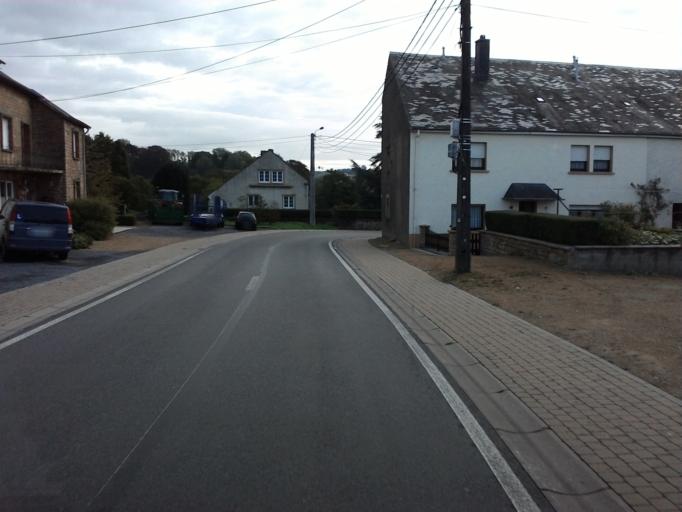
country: BE
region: Wallonia
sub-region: Province du Luxembourg
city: Virton
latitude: 49.5638
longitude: 5.5938
